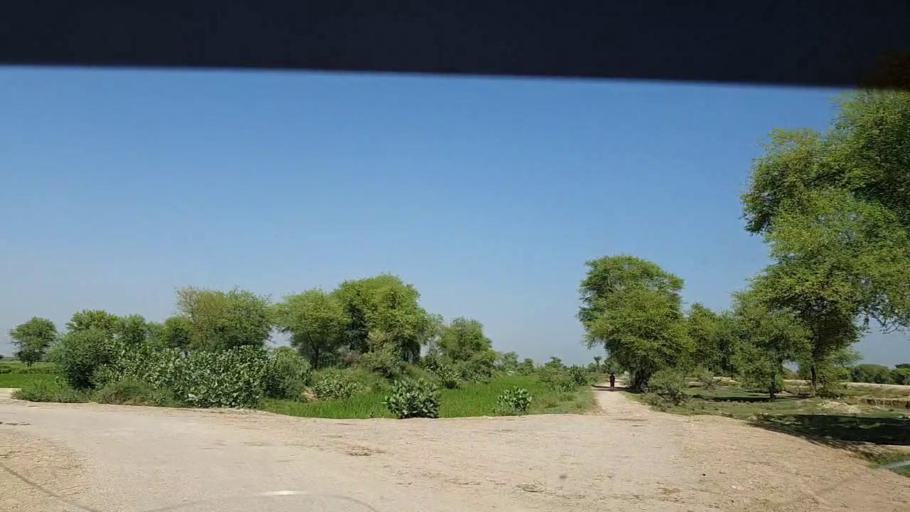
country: PK
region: Sindh
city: Kandhkot
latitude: 28.3041
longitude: 69.1124
